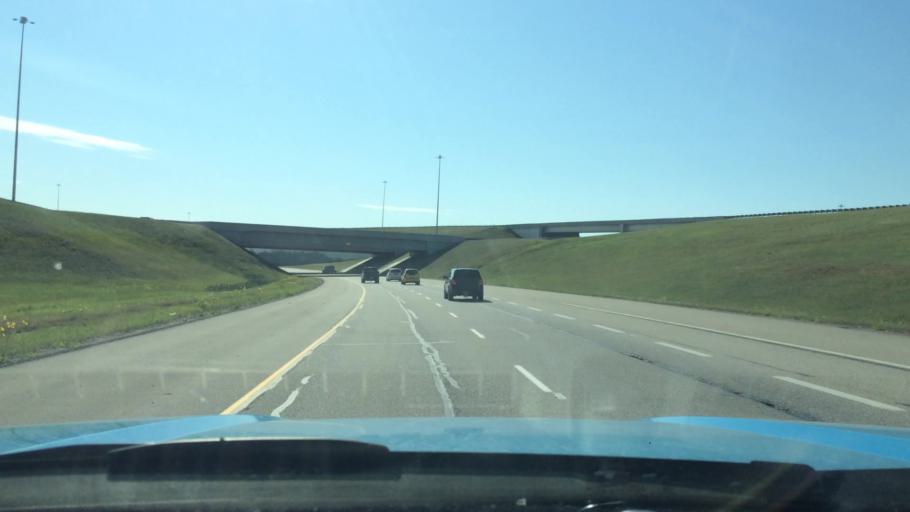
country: CA
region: Alberta
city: Airdrie
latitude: 51.1745
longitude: -114.0040
